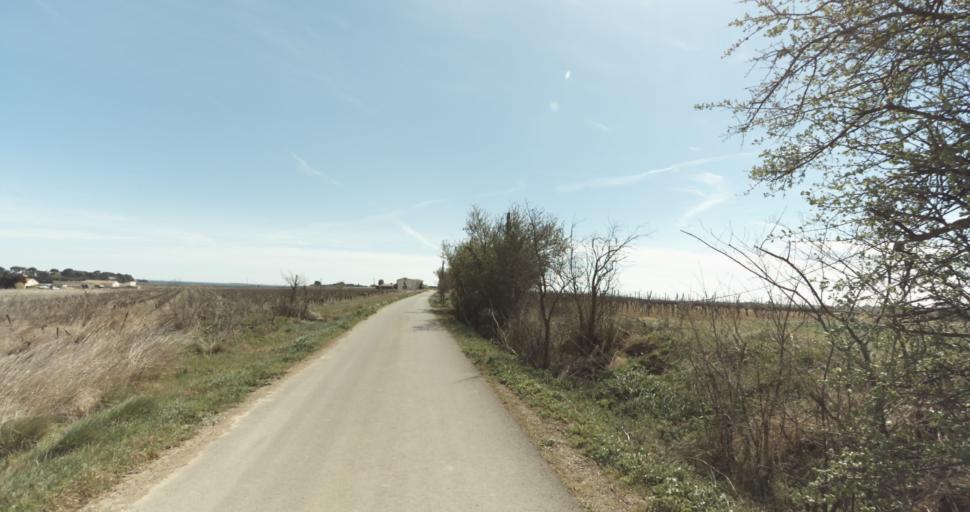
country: FR
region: Languedoc-Roussillon
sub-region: Departement de l'Herault
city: Pinet
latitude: 43.4088
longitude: 3.5470
